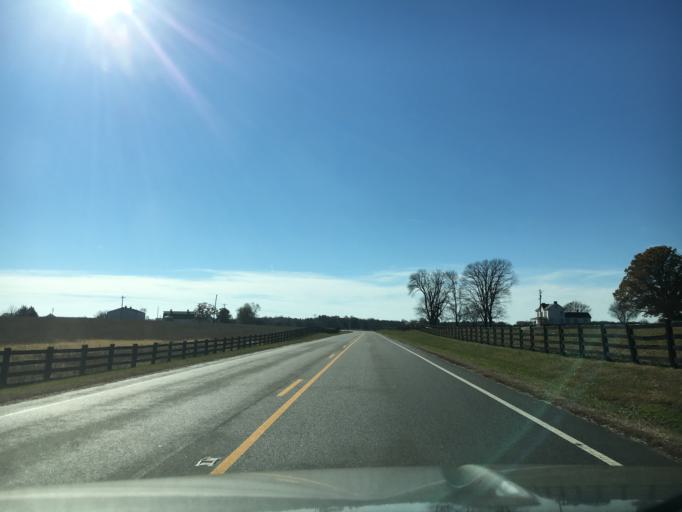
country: US
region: Virginia
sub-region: Cumberland County
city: Cumberland
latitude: 37.5771
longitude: -78.1756
